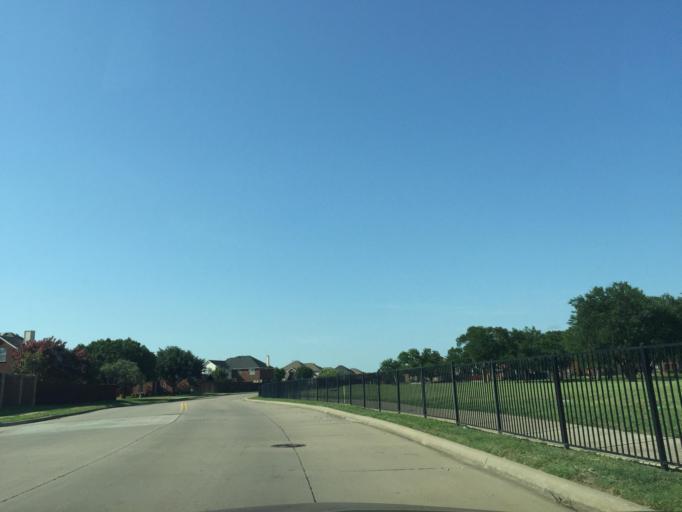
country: US
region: Texas
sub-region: Denton County
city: Lewisville
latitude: 33.0126
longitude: -96.9364
